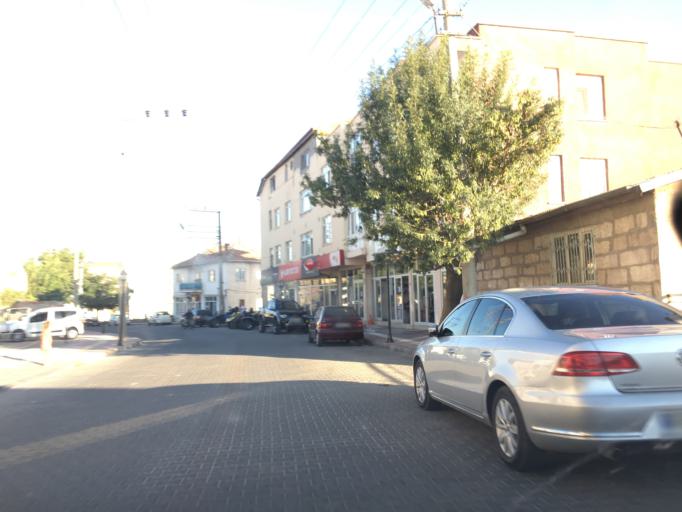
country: TR
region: Nevsehir
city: Avanos
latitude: 38.7181
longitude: 34.8412
